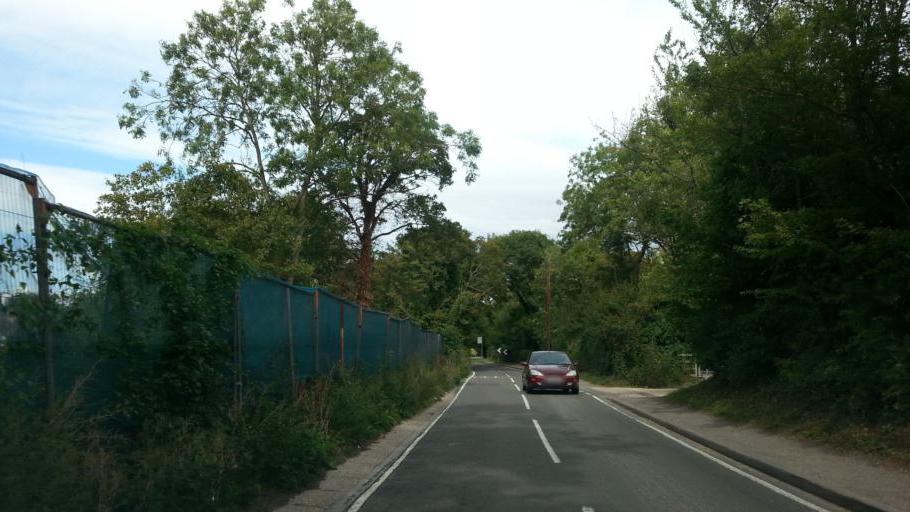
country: GB
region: England
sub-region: Cambridgeshire
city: Fulbourn
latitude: 52.1821
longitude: 0.1698
